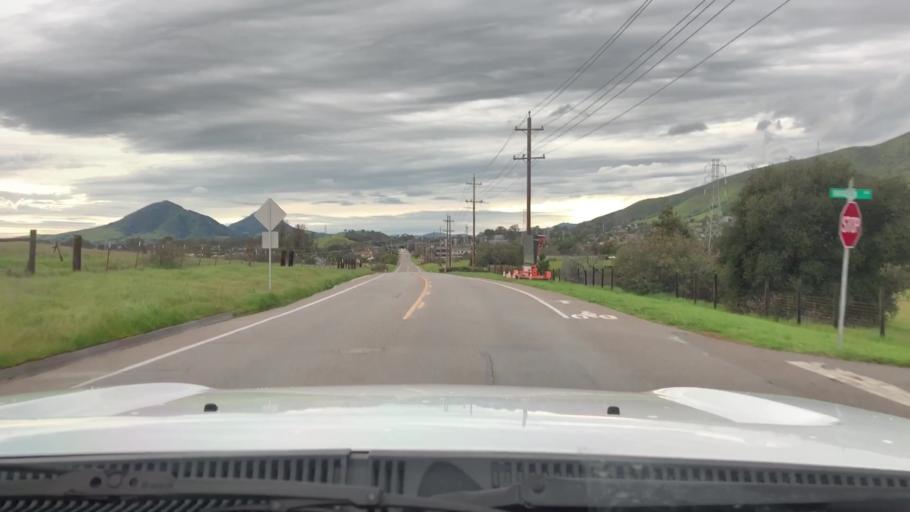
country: US
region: California
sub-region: San Luis Obispo County
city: San Luis Obispo
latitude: 35.2541
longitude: -120.6283
